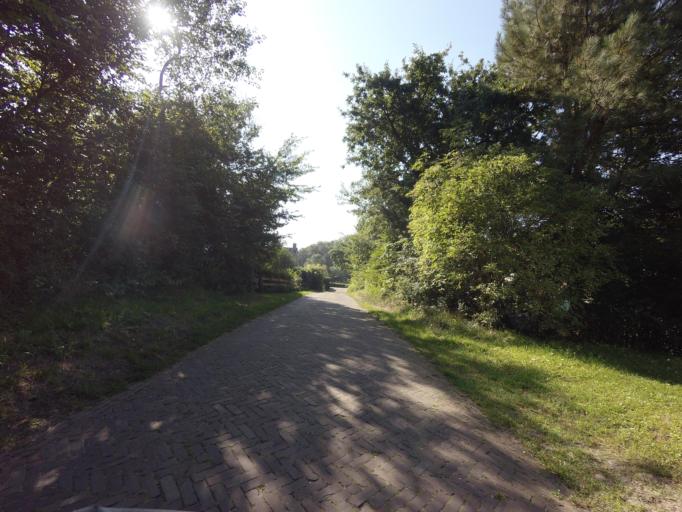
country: NL
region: Friesland
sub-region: Gemeente Schiermonnikoog
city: Schiermonnikoog
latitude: 53.4814
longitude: 6.1667
